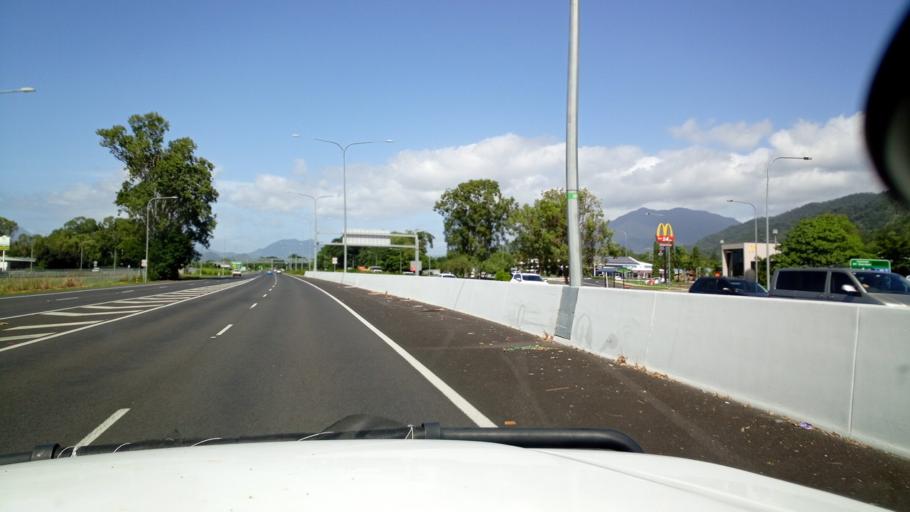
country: AU
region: Queensland
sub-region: Cairns
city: Woree
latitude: -16.9615
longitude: 145.7470
